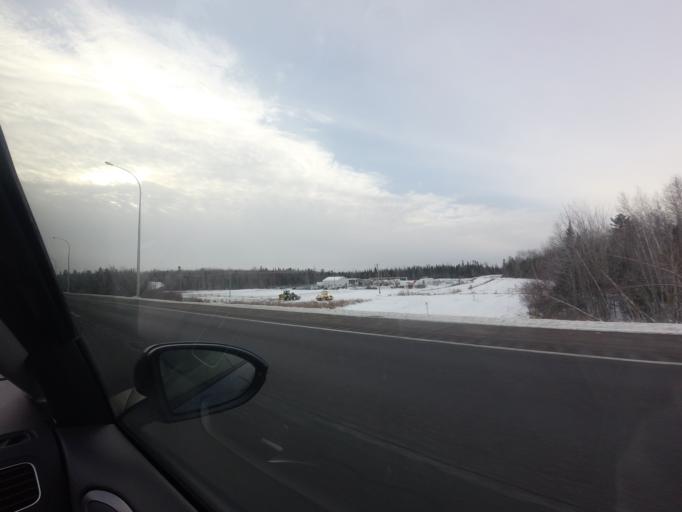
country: CA
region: New Brunswick
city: Oromocto
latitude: 45.8622
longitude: -66.5823
